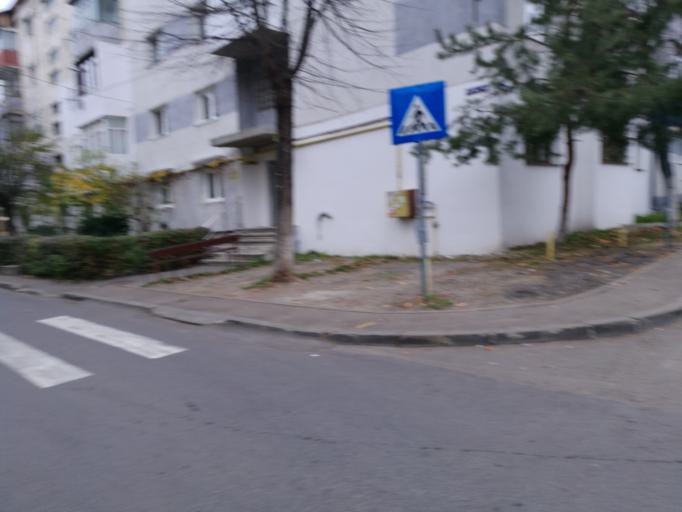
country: RO
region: Suceava
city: Suceava
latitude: 47.6721
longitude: 26.2767
